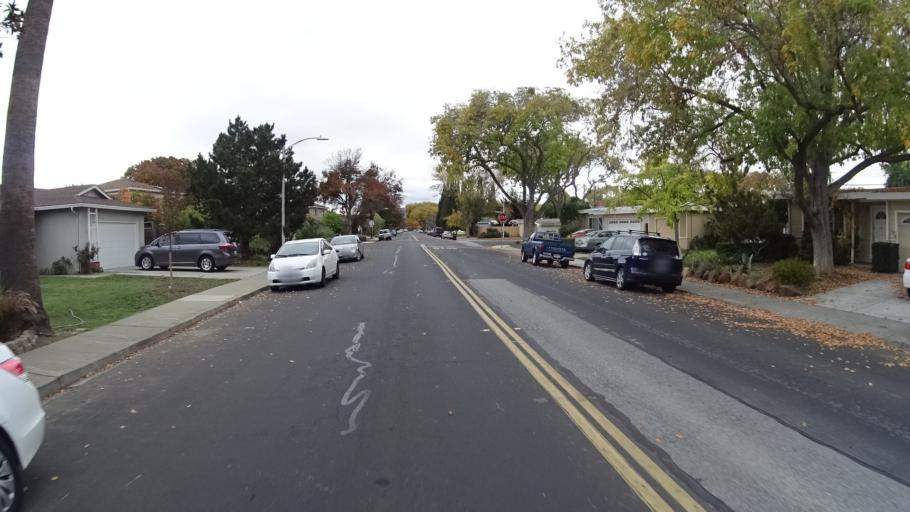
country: US
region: California
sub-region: Santa Clara County
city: Santa Clara
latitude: 37.3357
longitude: -121.9797
